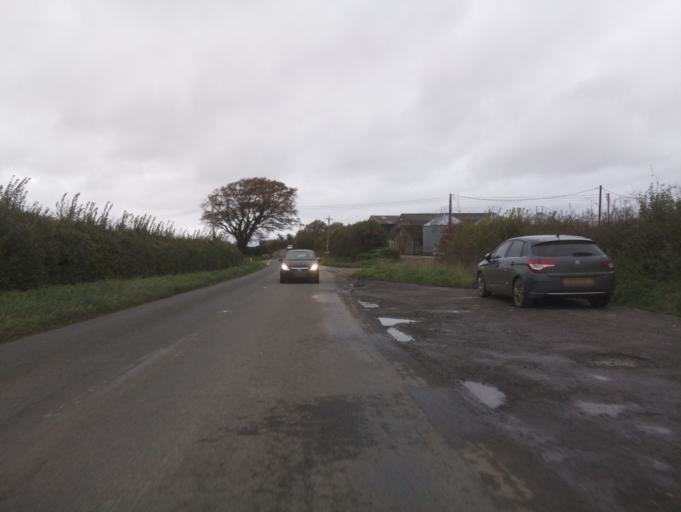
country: GB
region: England
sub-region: Dorset
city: Sherborne
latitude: 50.9786
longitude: -2.5630
